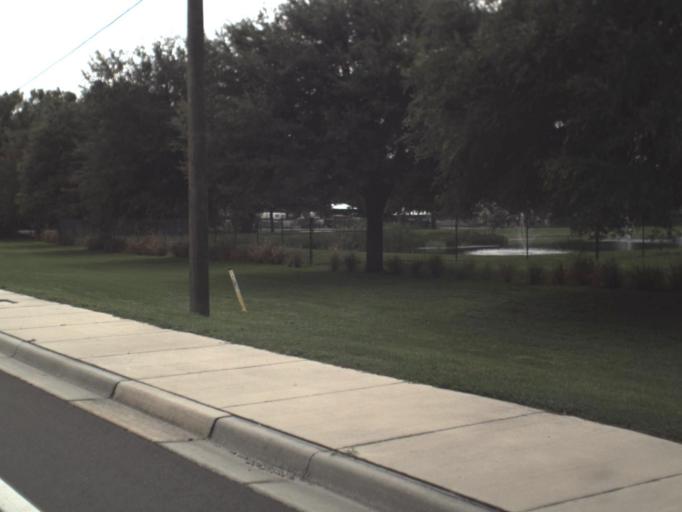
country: US
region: Florida
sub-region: Manatee County
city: Ellenton
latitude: 27.5714
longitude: -82.4256
